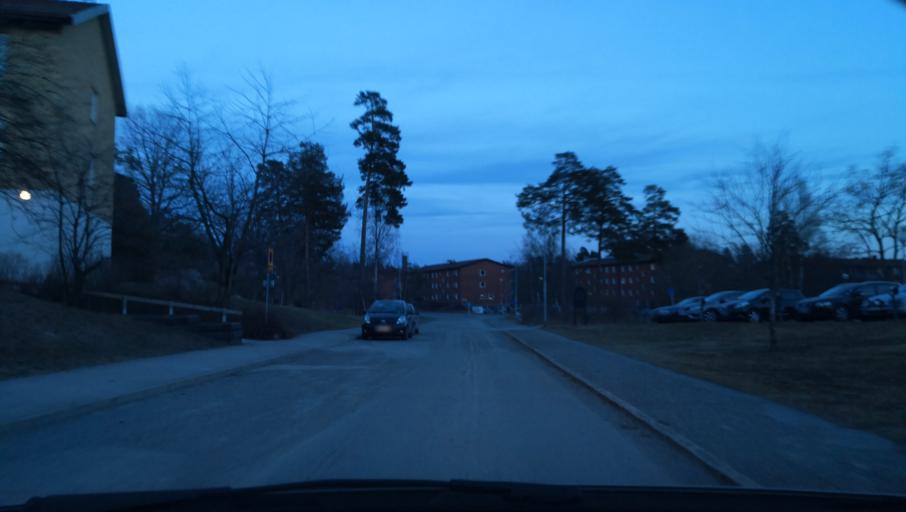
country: SE
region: Stockholm
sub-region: Varmdo Kommun
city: Gustavsberg
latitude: 59.3365
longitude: 18.3925
